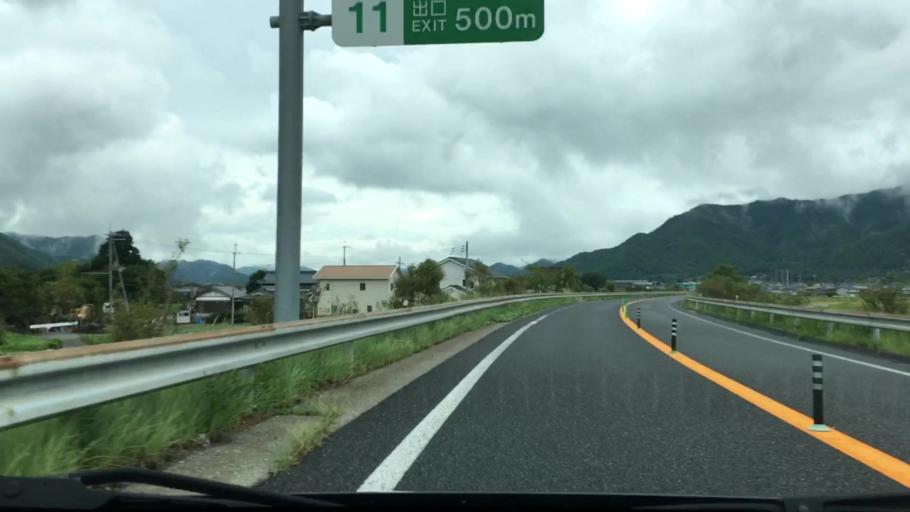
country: JP
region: Hyogo
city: Nishiwaki
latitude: 35.0636
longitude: 134.7673
